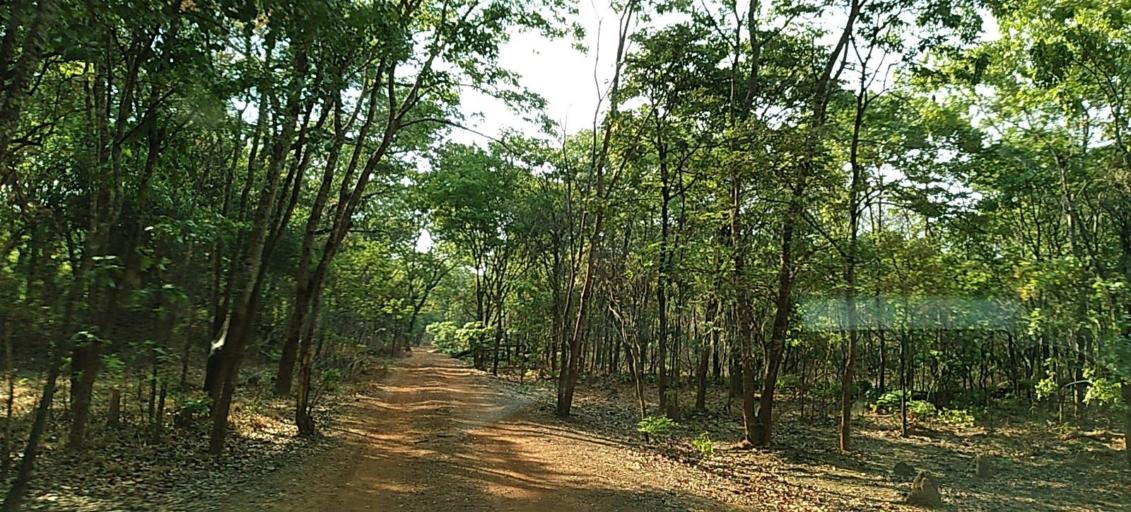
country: ZM
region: Copperbelt
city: Kalulushi
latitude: -13.0011
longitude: 27.7119
